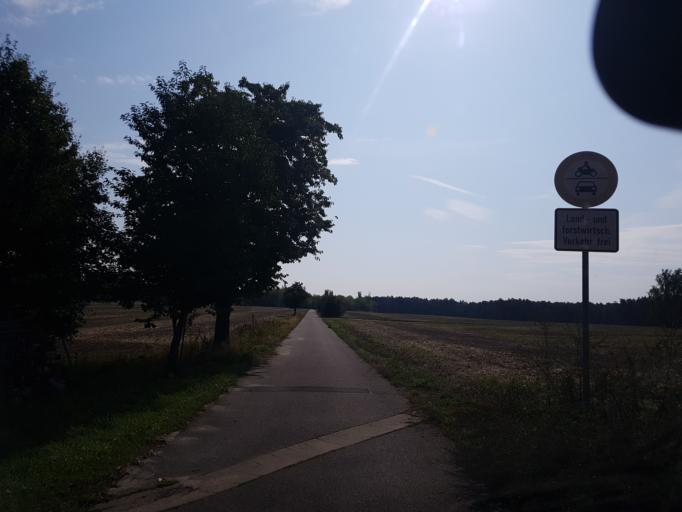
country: DE
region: Brandenburg
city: Plessa
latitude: 51.5300
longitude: 13.6356
